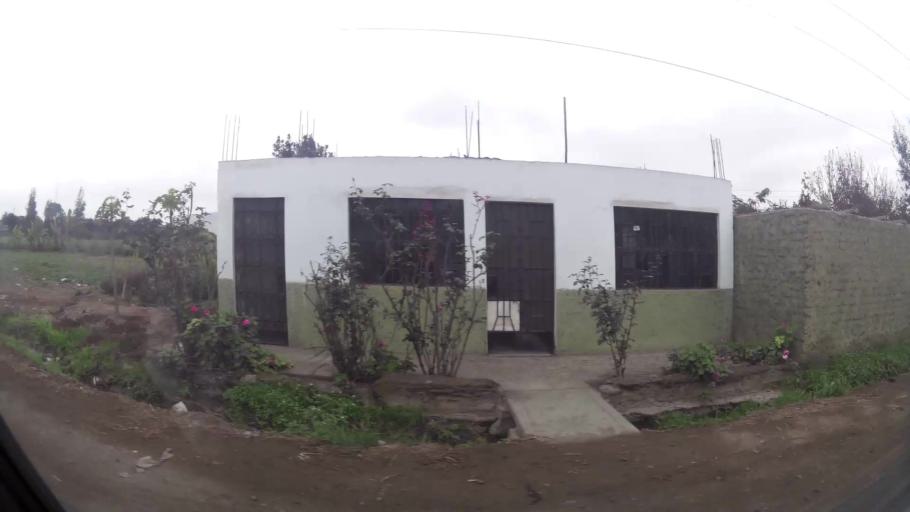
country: PE
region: Lima
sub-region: Provincia de Huaral
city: Chancay
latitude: -11.5258
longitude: -77.2475
